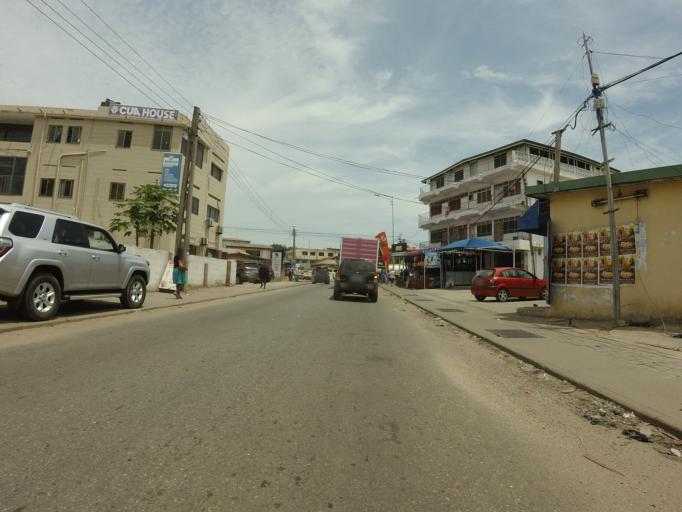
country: GH
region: Greater Accra
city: Accra
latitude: 5.5553
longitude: -0.2108
